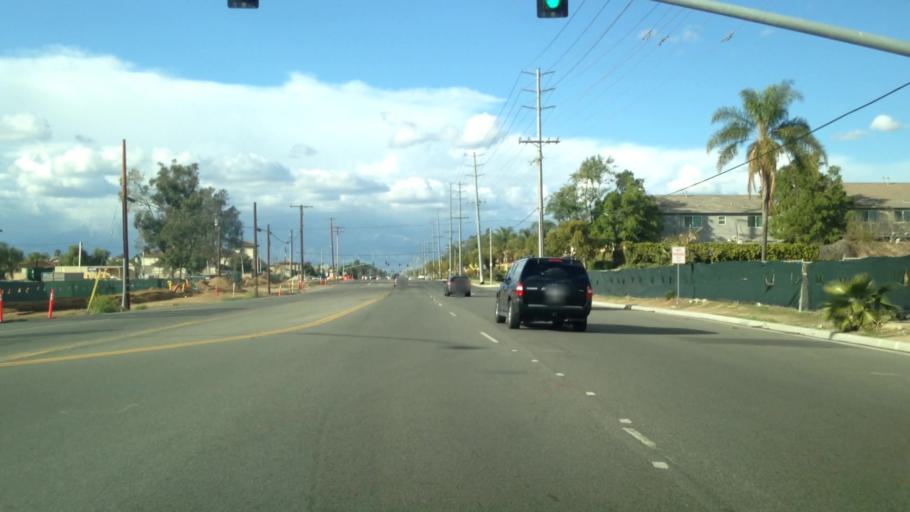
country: US
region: California
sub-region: Riverside County
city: Norco
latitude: 33.9570
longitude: -117.5583
